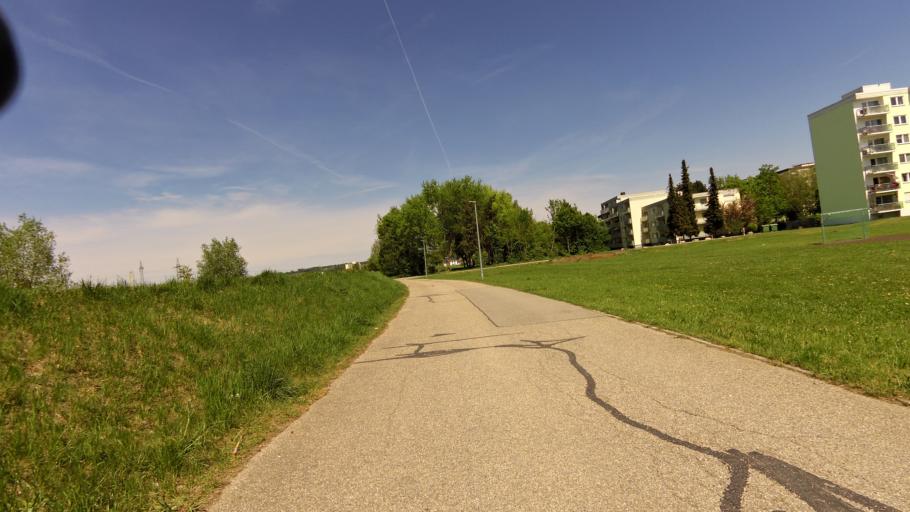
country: DE
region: Bavaria
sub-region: Lower Bavaria
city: Tiefenbach
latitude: 48.5472
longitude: 12.1151
